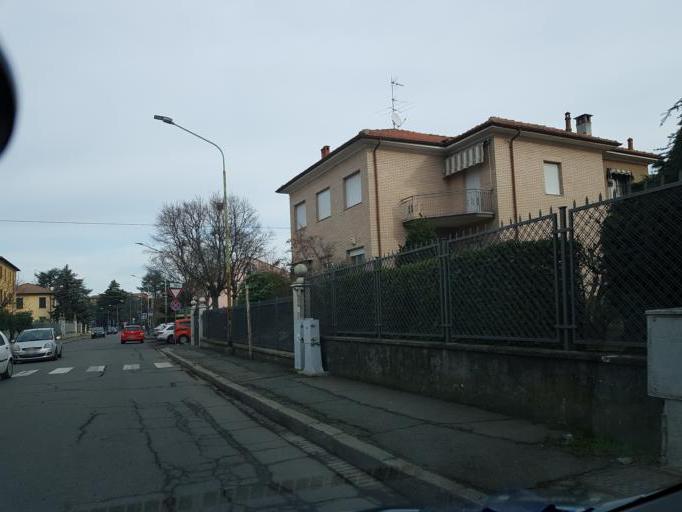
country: IT
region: Piedmont
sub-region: Provincia di Alessandria
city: Novi Ligure
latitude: 44.7644
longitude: 8.7969
